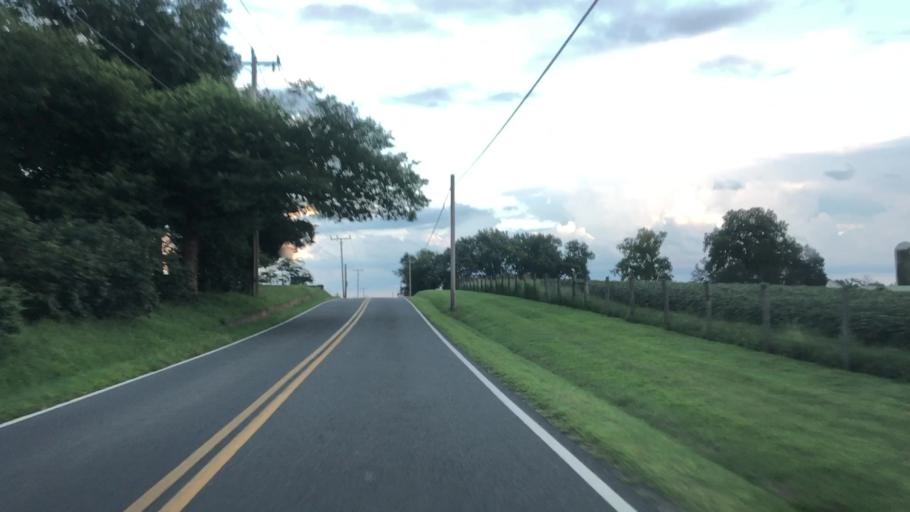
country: US
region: Virginia
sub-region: Prince William County
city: Nokesville
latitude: 38.6492
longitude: -77.6375
